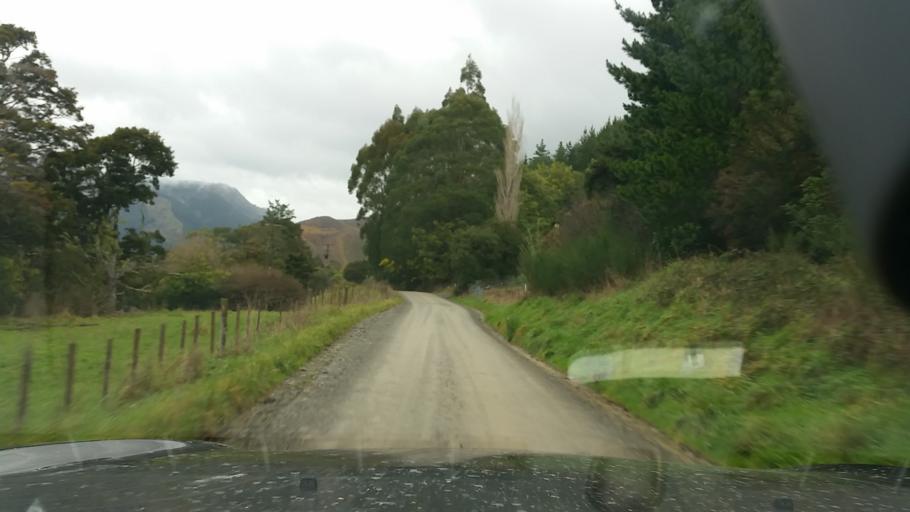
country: NZ
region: Marlborough
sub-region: Marlborough District
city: Picton
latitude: -41.2973
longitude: 173.6643
